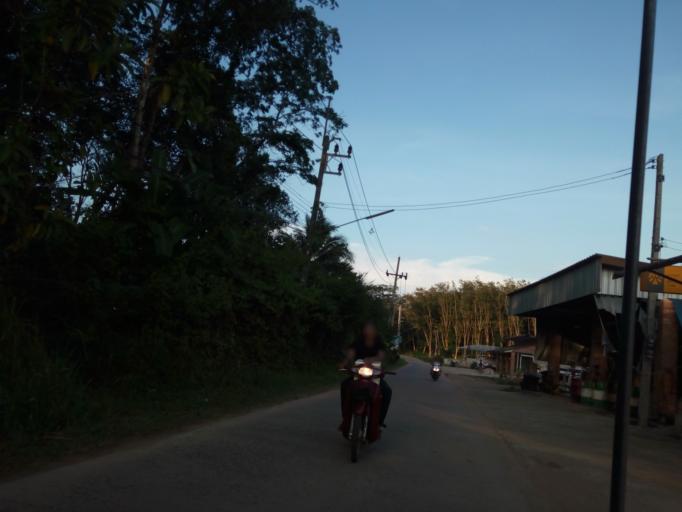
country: TH
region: Phangnga
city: Ko Yao
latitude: 8.0952
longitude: 98.6159
